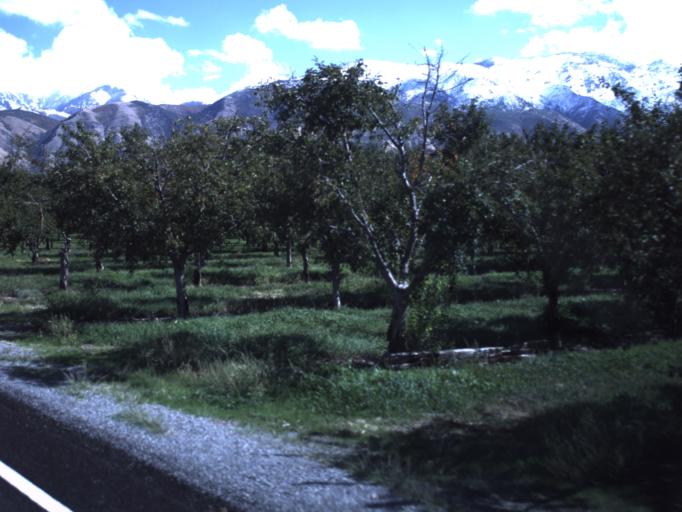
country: US
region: Utah
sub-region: Utah County
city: West Mountain
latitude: 40.0191
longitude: -111.7944
